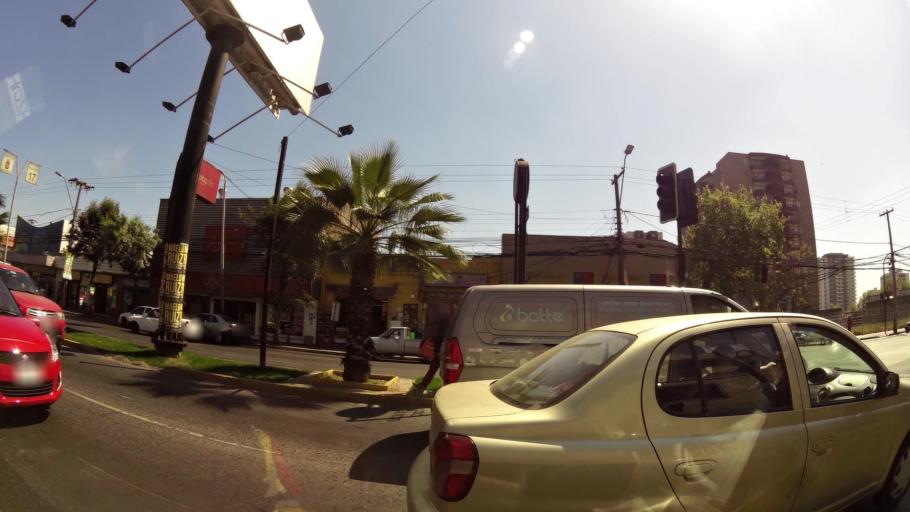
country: CL
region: Santiago Metropolitan
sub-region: Provincia de Santiago
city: Santiago
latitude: -33.5148
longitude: -70.6582
